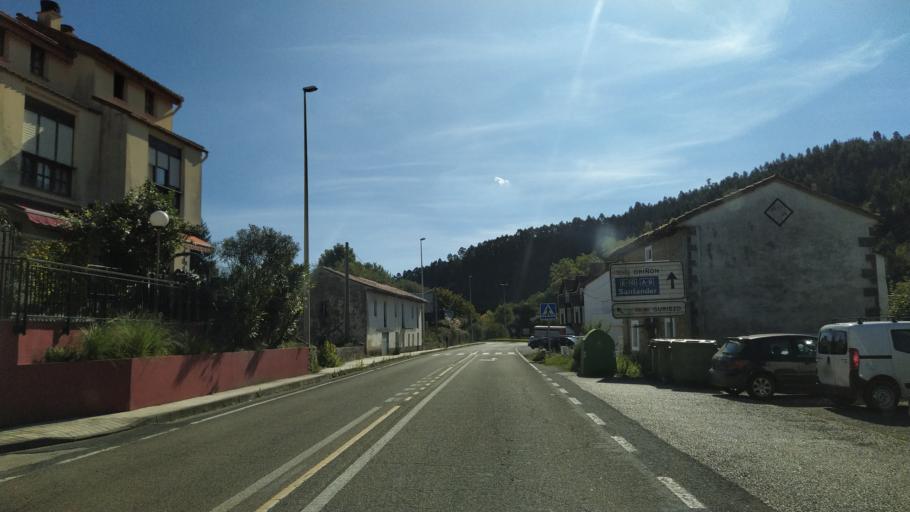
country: ES
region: Cantabria
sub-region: Provincia de Cantabria
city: Liendo
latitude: 43.3805
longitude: -3.3203
